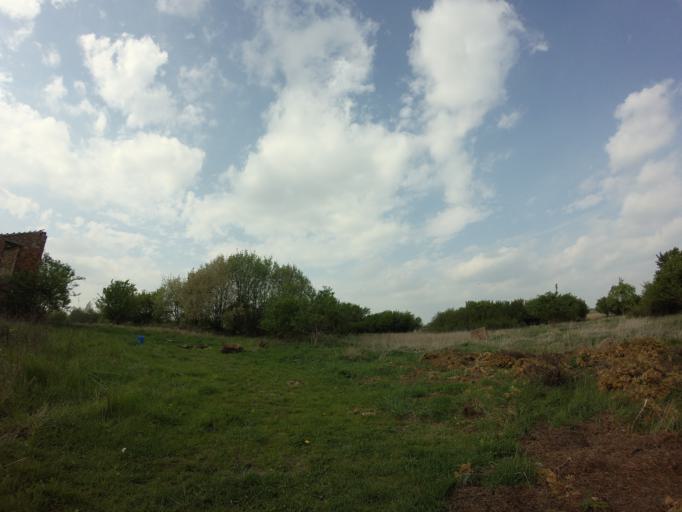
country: PL
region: West Pomeranian Voivodeship
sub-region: Powiat choszczenski
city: Choszczno
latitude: 53.1721
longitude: 15.3915
